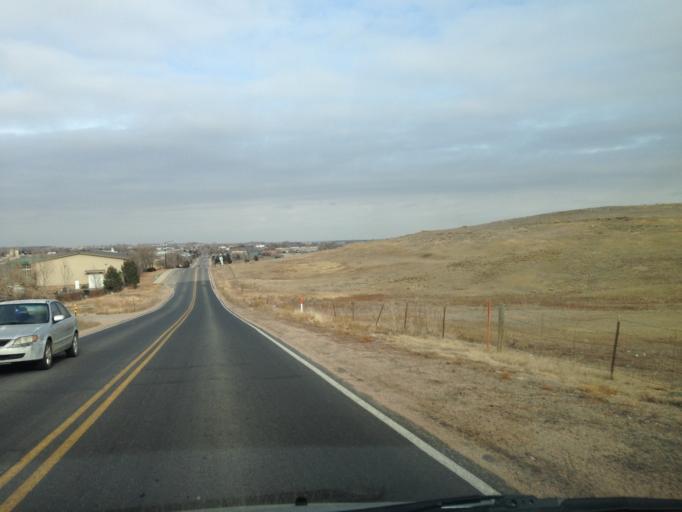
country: US
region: Colorado
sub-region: Boulder County
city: Lafayette
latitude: 39.9709
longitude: -105.0719
